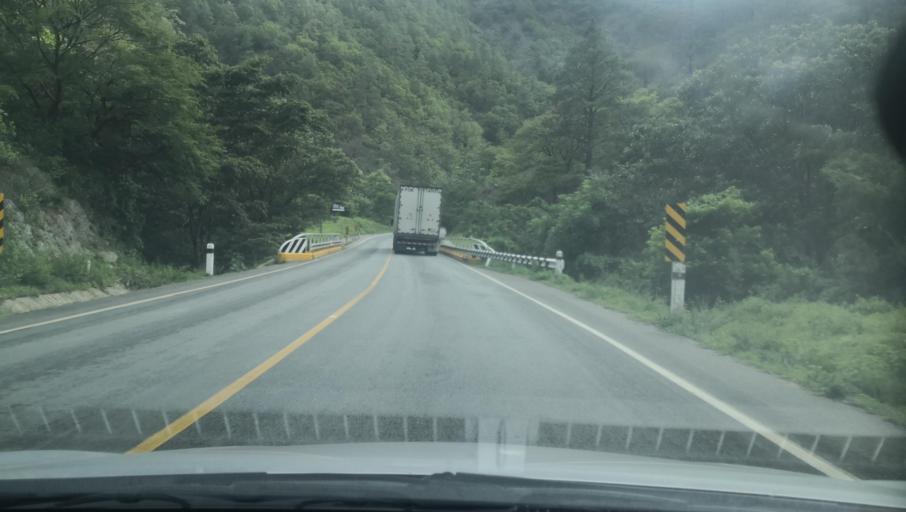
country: NI
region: Nueva Segovia
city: Mozonte
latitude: 13.7119
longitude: -86.5022
